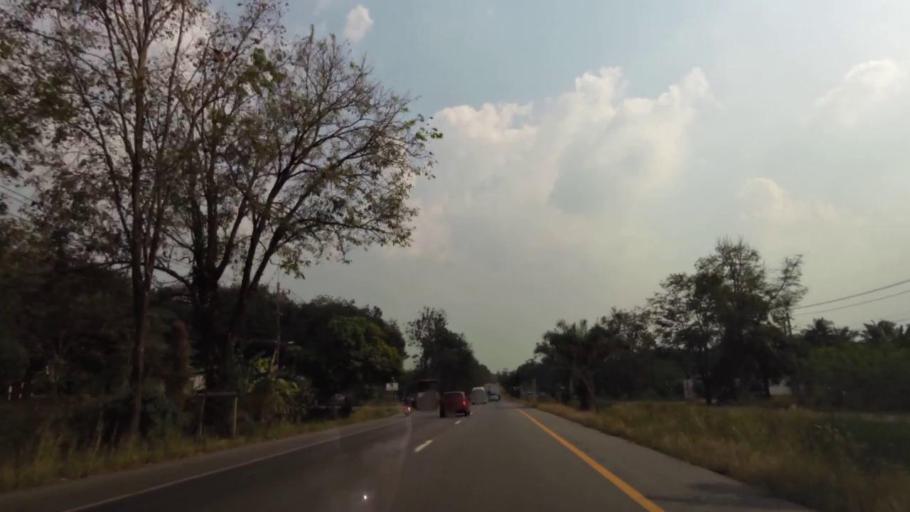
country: TH
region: Chon Buri
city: Nong Yai
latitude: 13.0826
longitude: 101.4016
